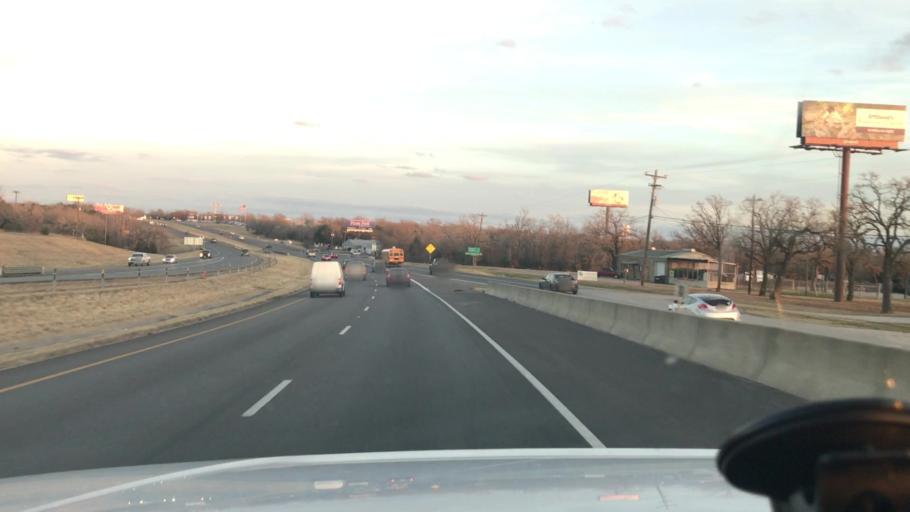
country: US
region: Texas
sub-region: Bastrop County
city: Wyldwood
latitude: 30.1113
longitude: -97.4130
